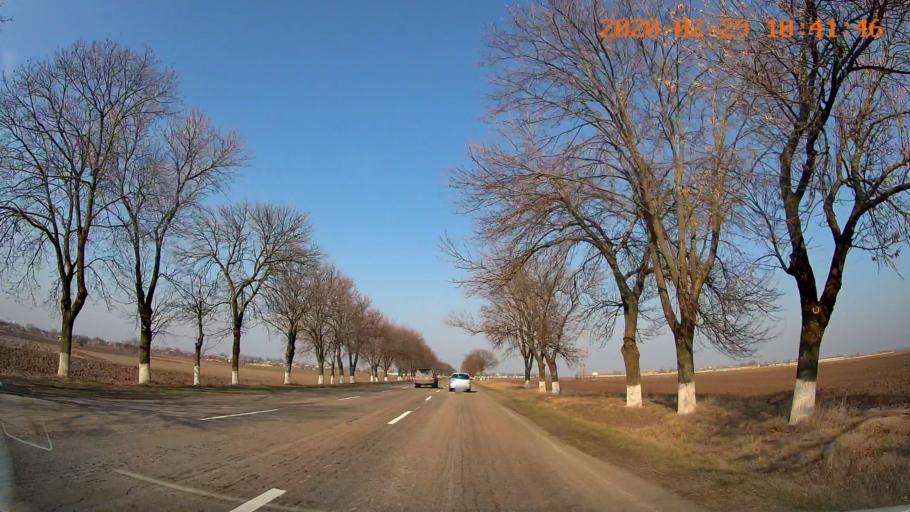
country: MD
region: Telenesti
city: Grigoriopol
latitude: 47.0455
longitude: 29.4204
